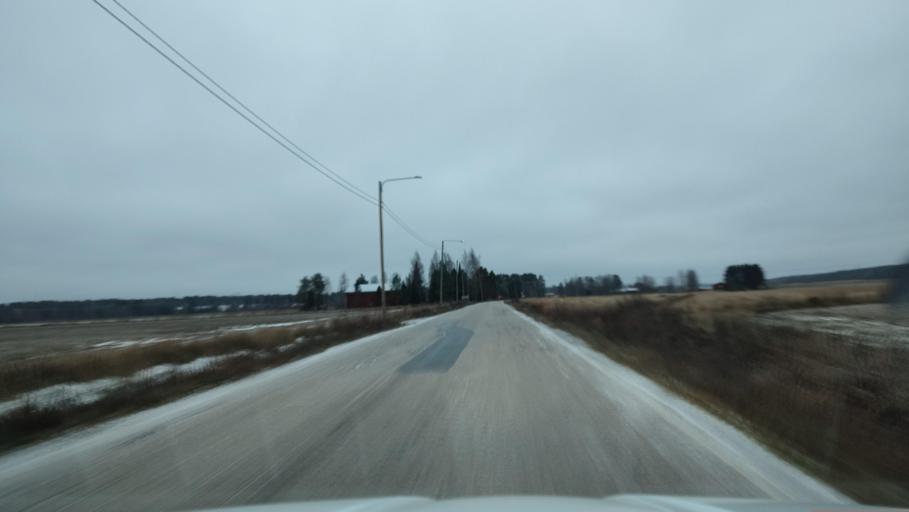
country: FI
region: Southern Ostrobothnia
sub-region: Suupohja
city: Karijoki
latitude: 62.2607
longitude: 21.6808
